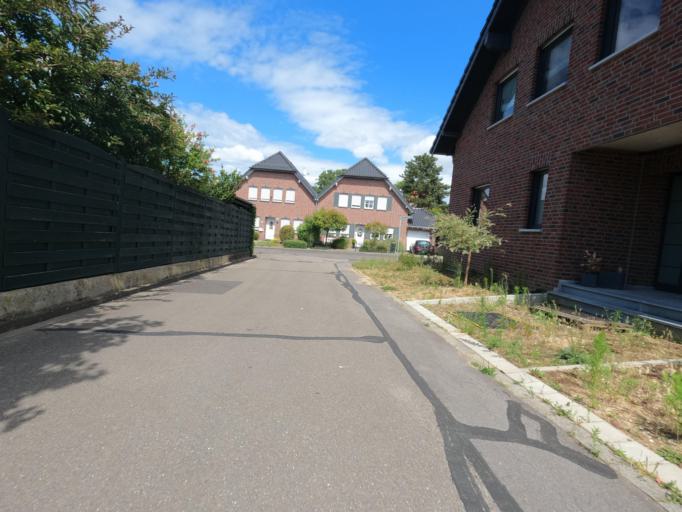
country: DE
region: North Rhine-Westphalia
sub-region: Regierungsbezirk Koln
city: Heinsberg
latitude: 51.0499
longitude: 6.1314
